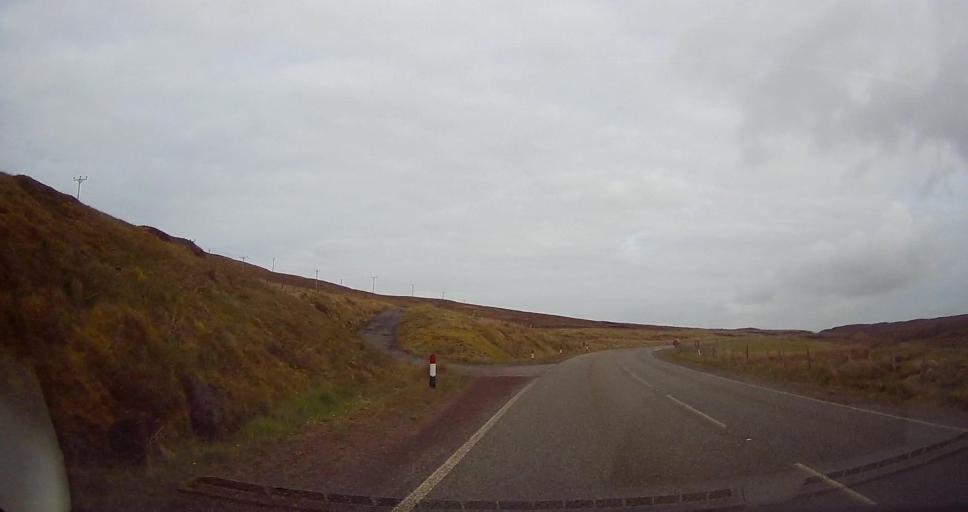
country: GB
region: Scotland
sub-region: Shetland Islands
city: Sandwick
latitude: 60.0837
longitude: -1.2318
